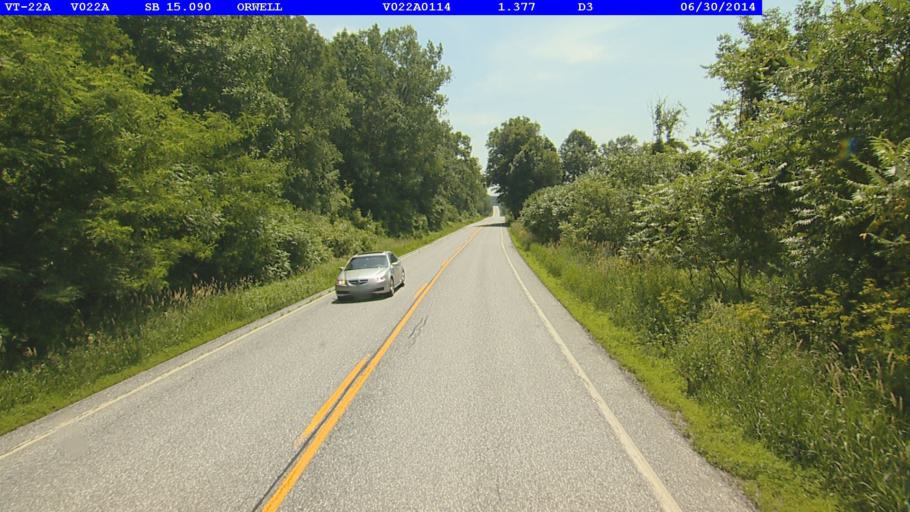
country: US
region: New York
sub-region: Essex County
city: Ticonderoga
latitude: 43.7769
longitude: -73.3080
